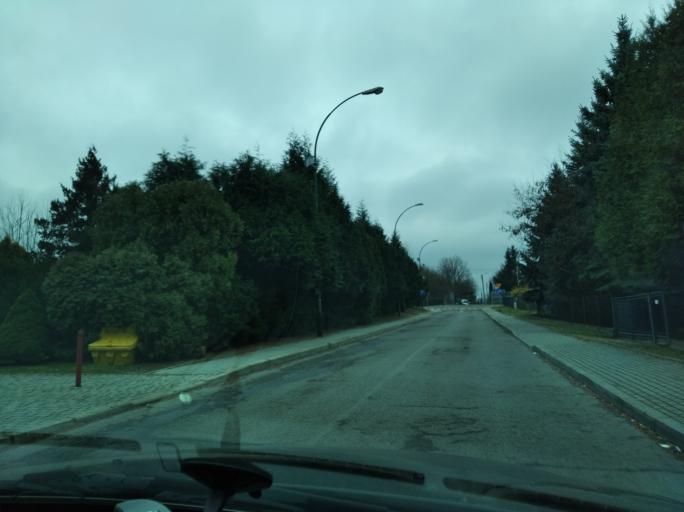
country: PL
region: Subcarpathian Voivodeship
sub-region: Powiat lancucki
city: Lancut
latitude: 50.0619
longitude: 22.2159
